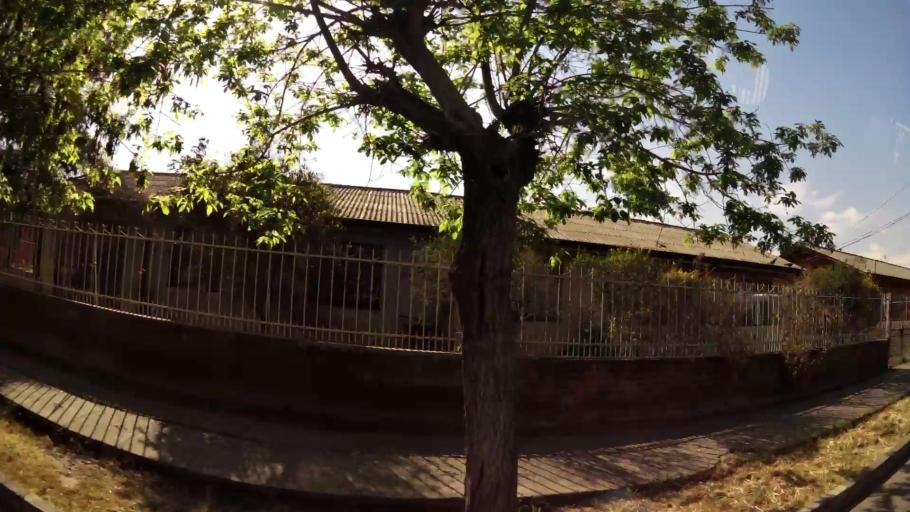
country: CL
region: Santiago Metropolitan
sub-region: Provincia de Santiago
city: La Pintana
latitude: -33.5559
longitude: -70.5908
